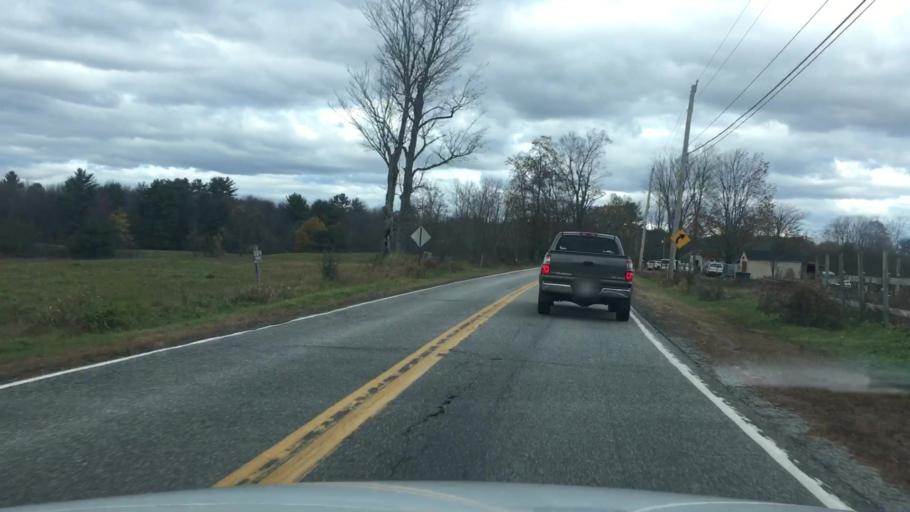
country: US
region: Maine
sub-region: Sagadahoc County
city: Richmond
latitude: 44.1130
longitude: -69.9105
